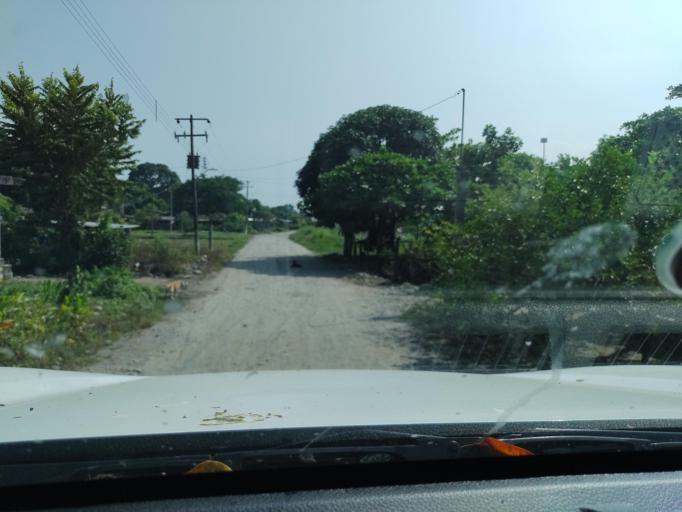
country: MX
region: Veracruz
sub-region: Martinez de la Torre
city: El Progreso
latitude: 20.0797
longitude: -97.0022
